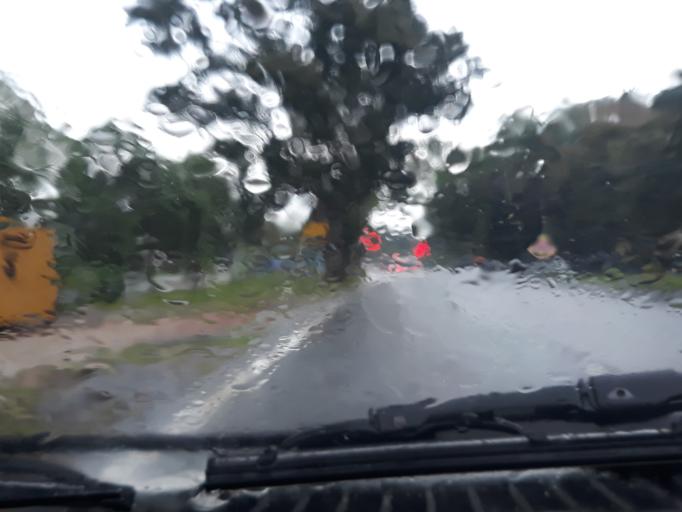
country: MY
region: Kedah
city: Kulim
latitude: 5.3712
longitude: 100.5813
